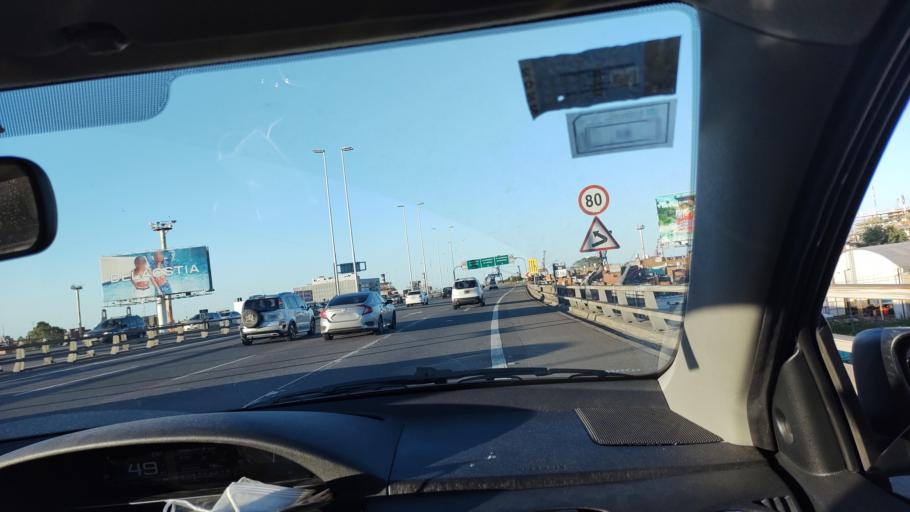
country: AR
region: Buenos Aires F.D.
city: Retiro
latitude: -34.5871
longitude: -58.3805
